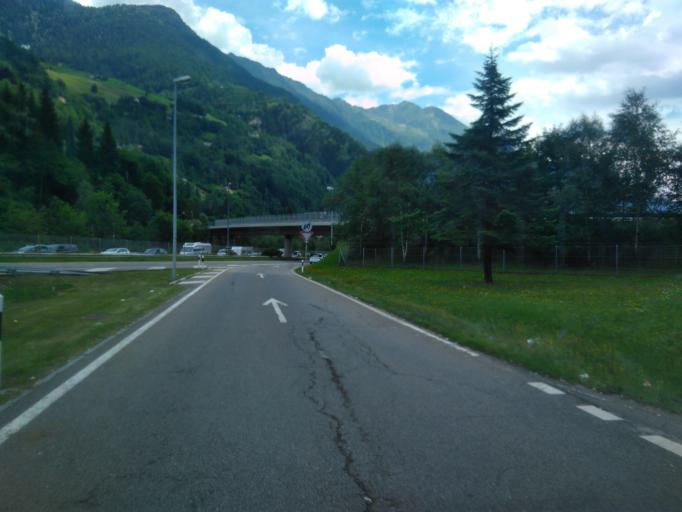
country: CH
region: Ticino
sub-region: Leventina District
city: Airolo
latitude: 46.5142
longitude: 8.6676
